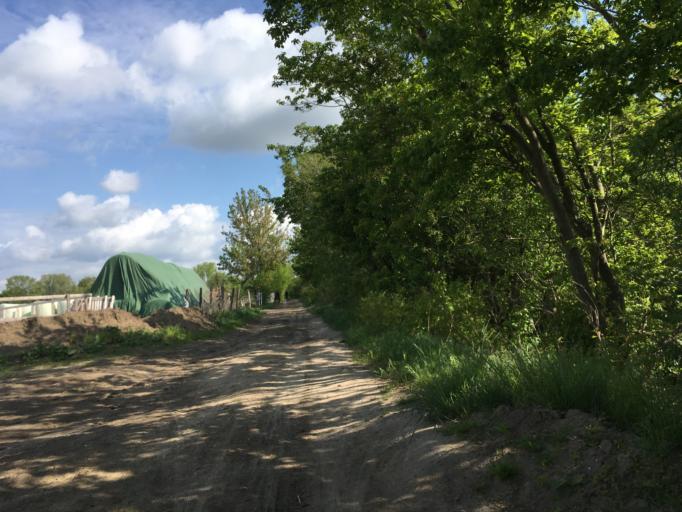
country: DE
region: Berlin
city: Blankenfelde
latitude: 52.6200
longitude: 13.4018
